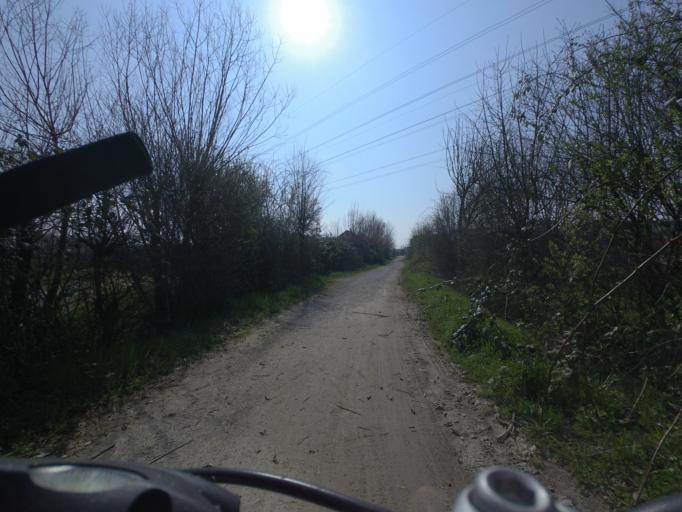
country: DE
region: Baden-Wuerttemberg
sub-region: Regierungsbezirk Stuttgart
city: Unterensingen
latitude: 48.6636
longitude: 9.3599
